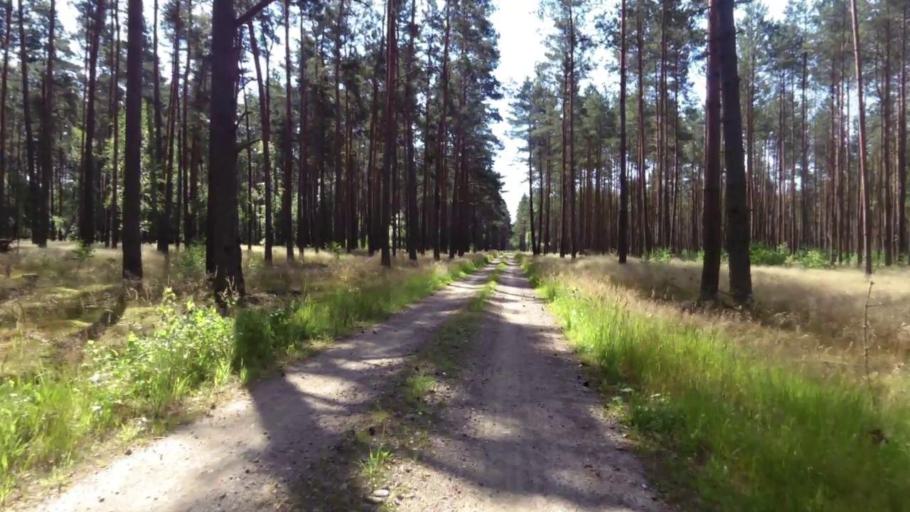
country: PL
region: West Pomeranian Voivodeship
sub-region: Powiat swidwinski
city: Polczyn-Zdroj
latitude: 53.8657
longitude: 16.1235
